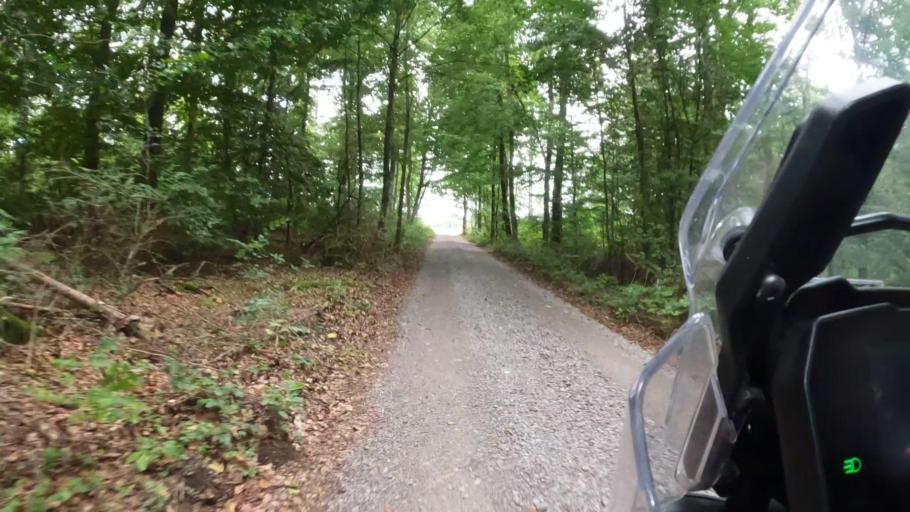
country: DE
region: Baden-Wuerttemberg
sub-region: Freiburg Region
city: Eggingen
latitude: 47.7075
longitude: 8.3628
